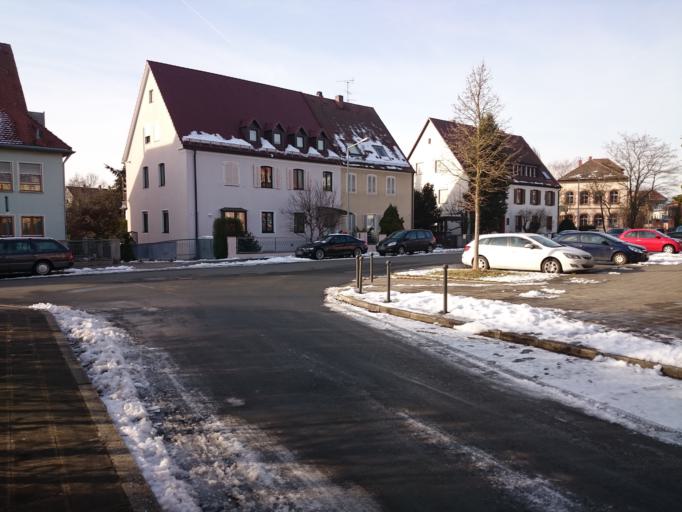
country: DE
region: Bavaria
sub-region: Regierungsbezirk Mittelfranken
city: Nuernberg
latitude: 49.4423
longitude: 11.1277
